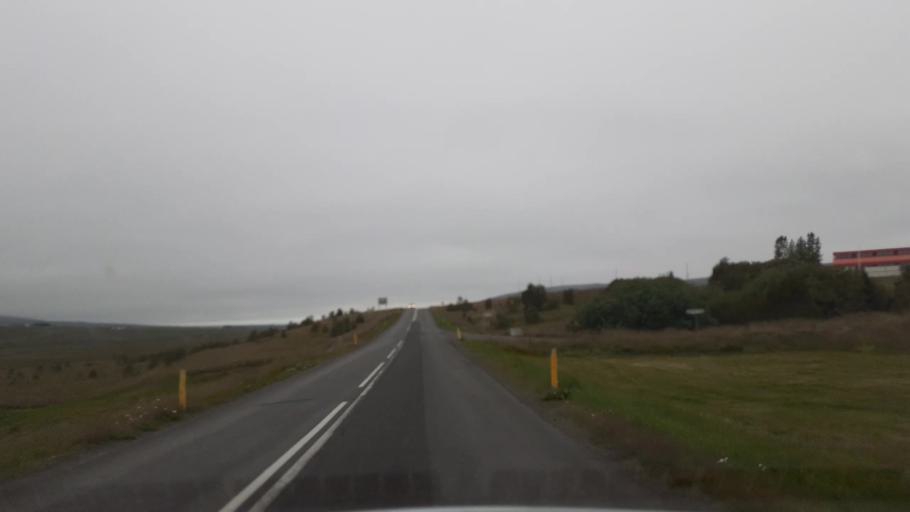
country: IS
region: Northeast
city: Siglufjoerdur
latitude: 65.7353
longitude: -19.1223
